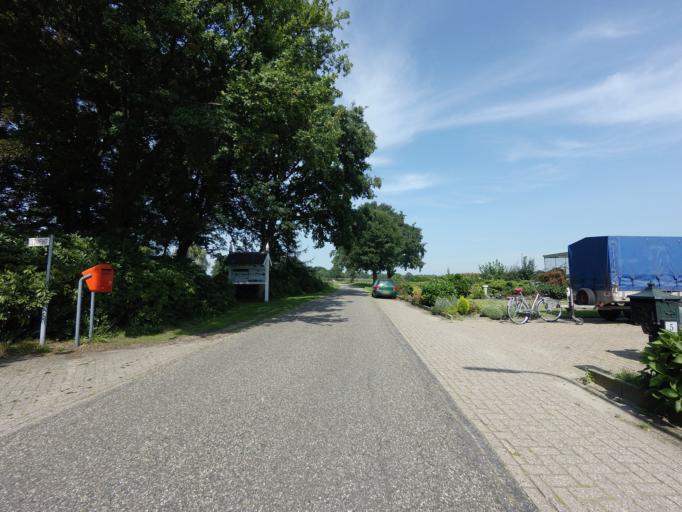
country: NL
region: Overijssel
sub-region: Gemeente Borne
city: Borne
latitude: 52.3102
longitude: 6.7145
